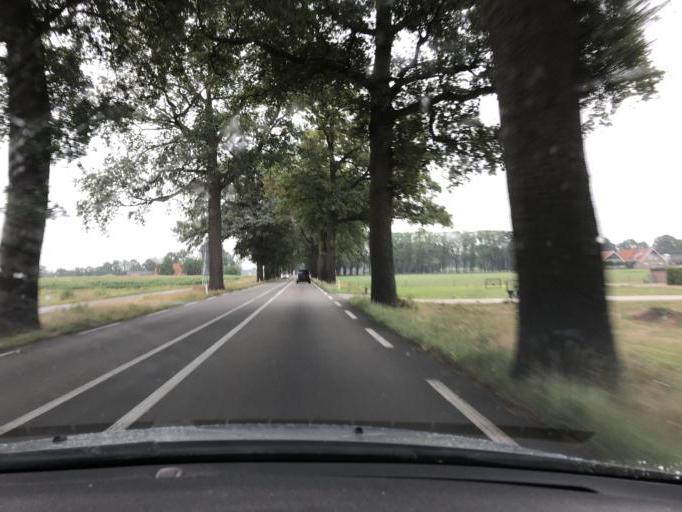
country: NL
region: Gelderland
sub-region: Berkelland
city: Eibergen
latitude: 52.0311
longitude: 6.6279
